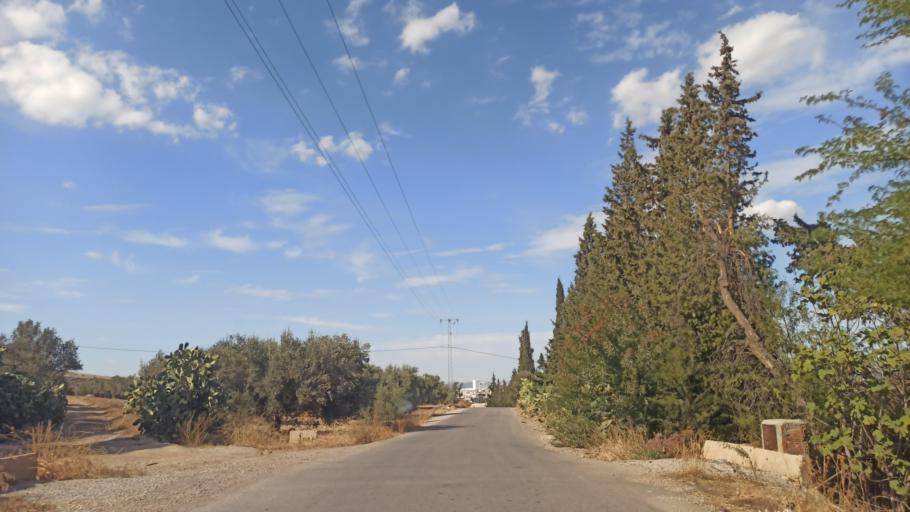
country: TN
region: Zaghwan
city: Zaghouan
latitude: 36.3387
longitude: 10.2096
